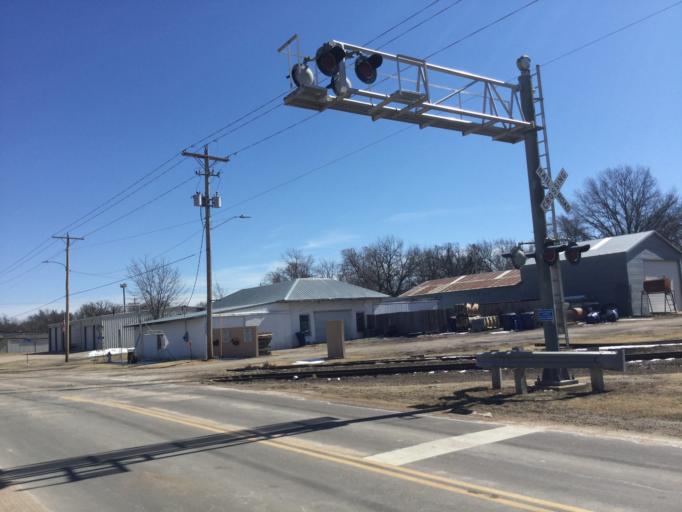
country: US
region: Kansas
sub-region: Sedgwick County
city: Clearwater
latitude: 37.5047
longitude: -97.5106
